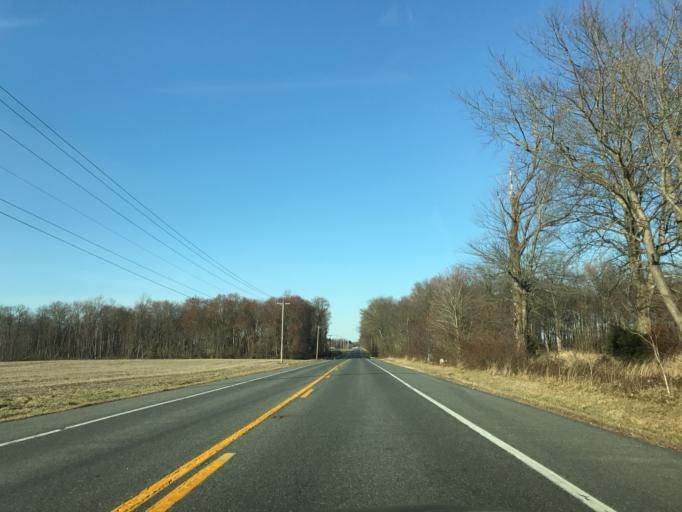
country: US
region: Maryland
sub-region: Queen Anne's County
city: Kingstown
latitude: 39.1663
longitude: -75.8610
